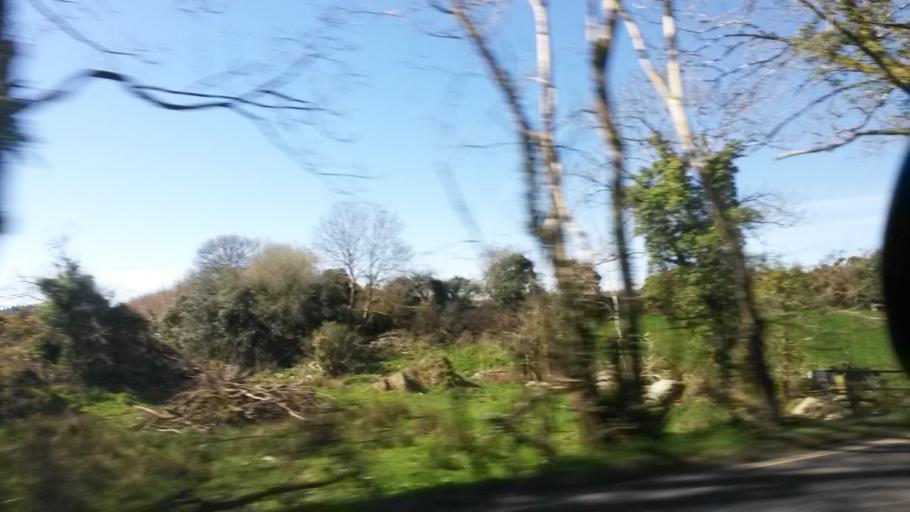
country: IE
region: Munster
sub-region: County Cork
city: Macroom
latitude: 51.9215
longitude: -9.0914
